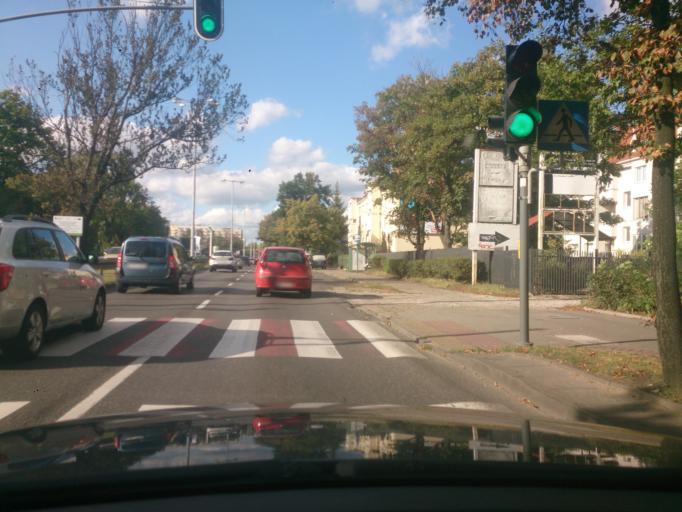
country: PL
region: Pomeranian Voivodeship
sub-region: Sopot
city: Sopot
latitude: 54.4271
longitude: 18.5629
